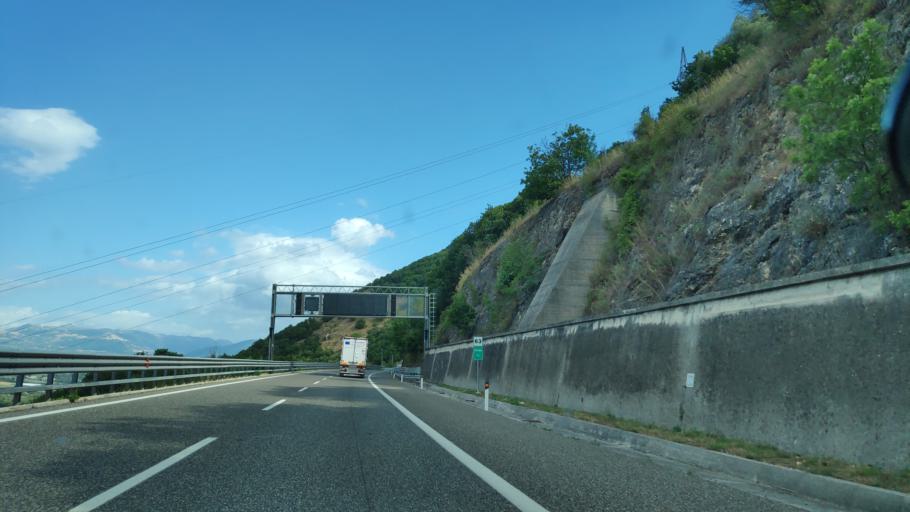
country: IT
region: Campania
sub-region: Provincia di Salerno
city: Sicignano degli Alburni
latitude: 40.5854
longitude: 15.3390
